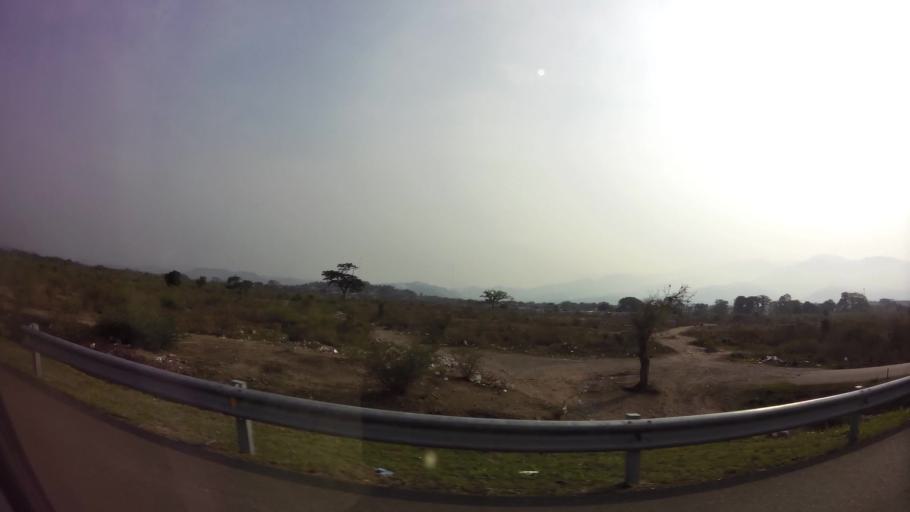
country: HN
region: Comayagua
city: Comayagua
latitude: 14.4310
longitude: -87.6453
